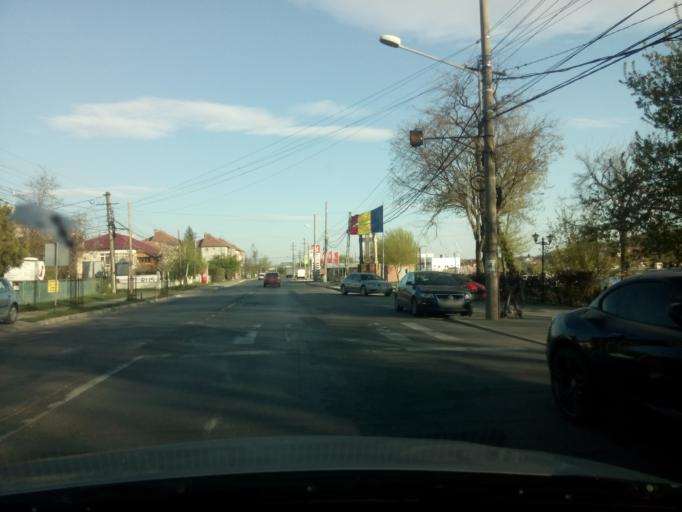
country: RO
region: Ilfov
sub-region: Comuna Mogosoaia
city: Mogosoaia
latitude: 44.5240
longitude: 26.0052
